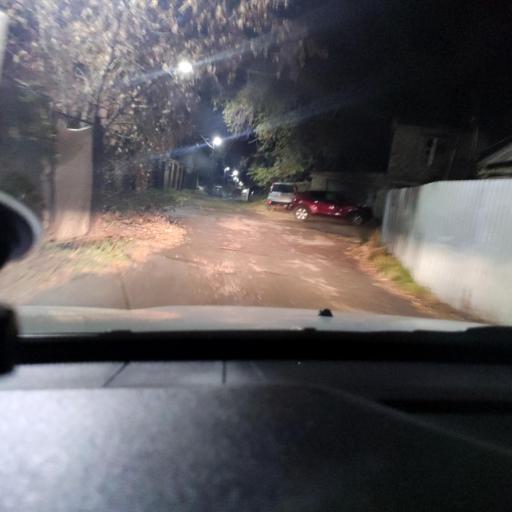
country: RU
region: Samara
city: Samara
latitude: 53.2267
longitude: 50.2208
